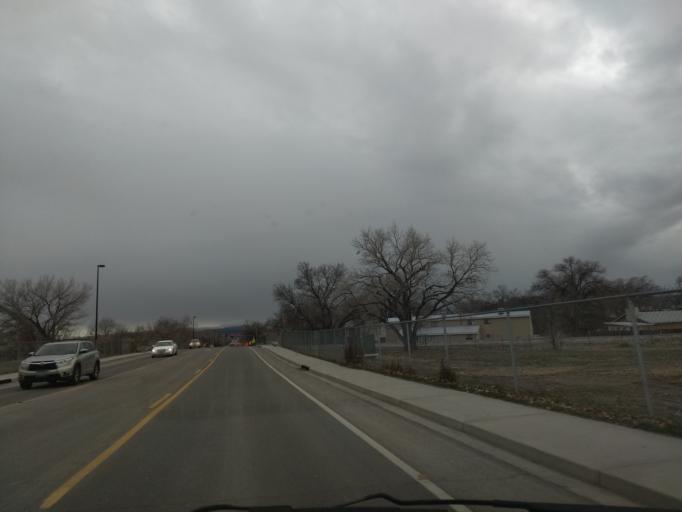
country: US
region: Colorado
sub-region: Mesa County
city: Fruitvale
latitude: 39.0869
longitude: -108.5153
